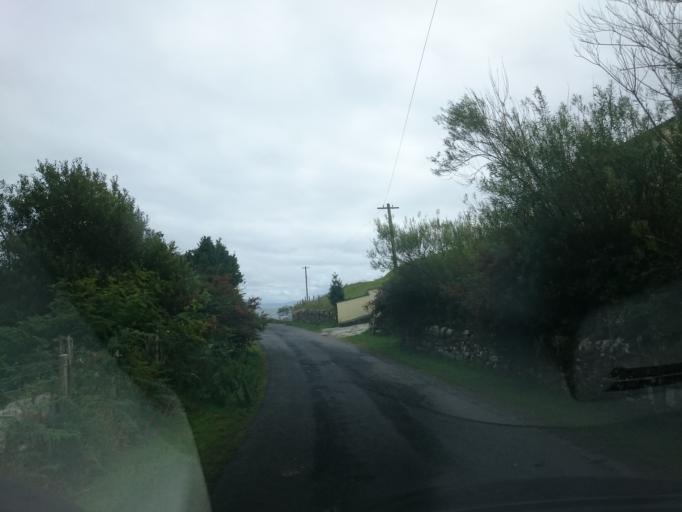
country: IE
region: Connaught
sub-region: Maigh Eo
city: Westport
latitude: 53.8995
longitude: -9.7902
